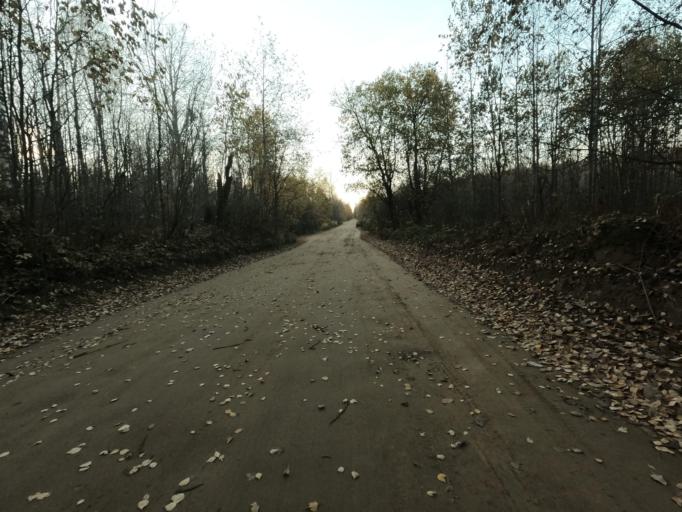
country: RU
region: Leningrad
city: Mga
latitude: 59.7555
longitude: 31.2783
